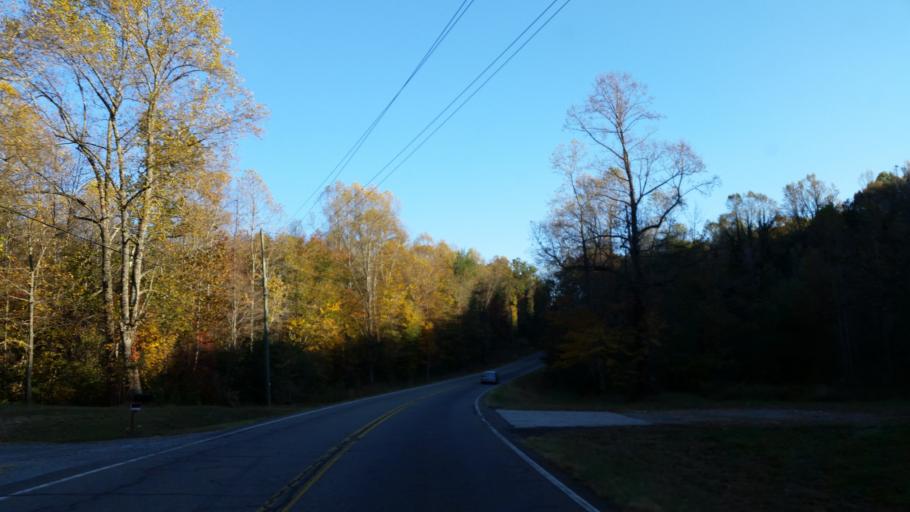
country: US
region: Georgia
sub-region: Pickens County
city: Jasper
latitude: 34.5912
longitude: -84.3092
